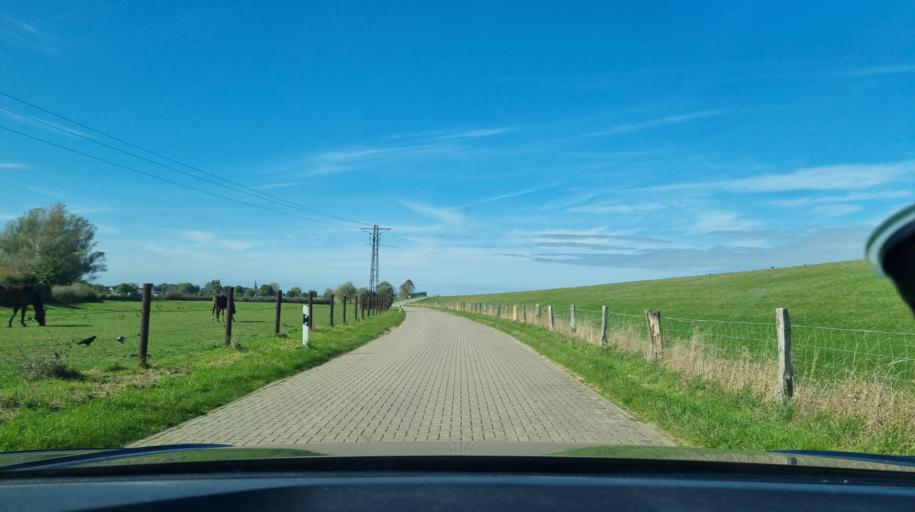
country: DE
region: North Rhine-Westphalia
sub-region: Regierungsbezirk Dusseldorf
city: Kleve
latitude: 51.8282
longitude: 6.1269
